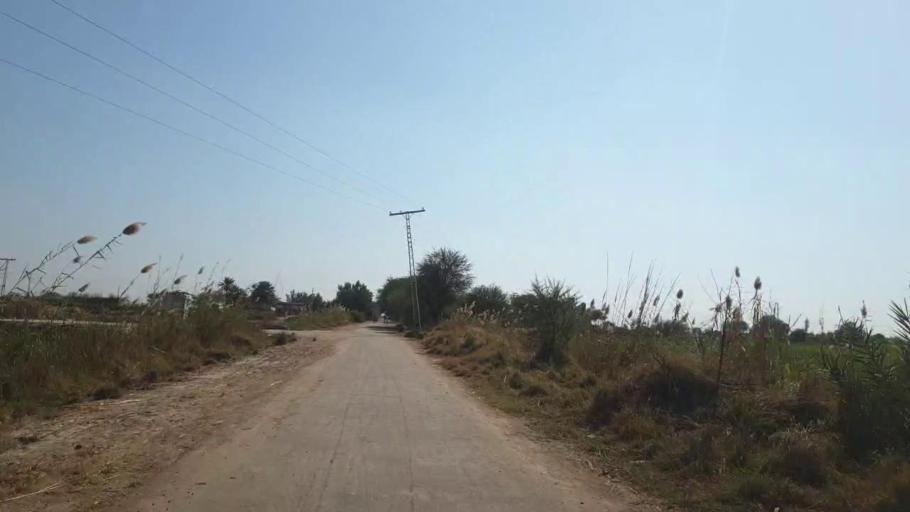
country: PK
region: Sindh
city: Mirpur Khas
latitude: 25.6396
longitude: 69.0280
